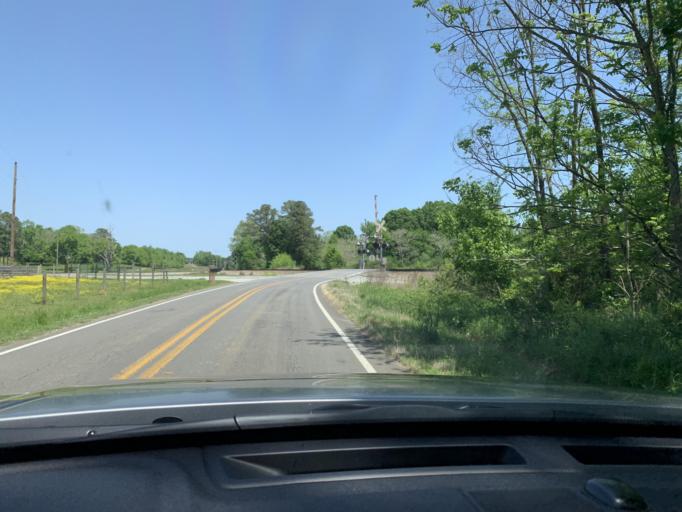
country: US
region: Georgia
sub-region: Polk County
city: Aragon
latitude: 34.0878
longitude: -85.1487
